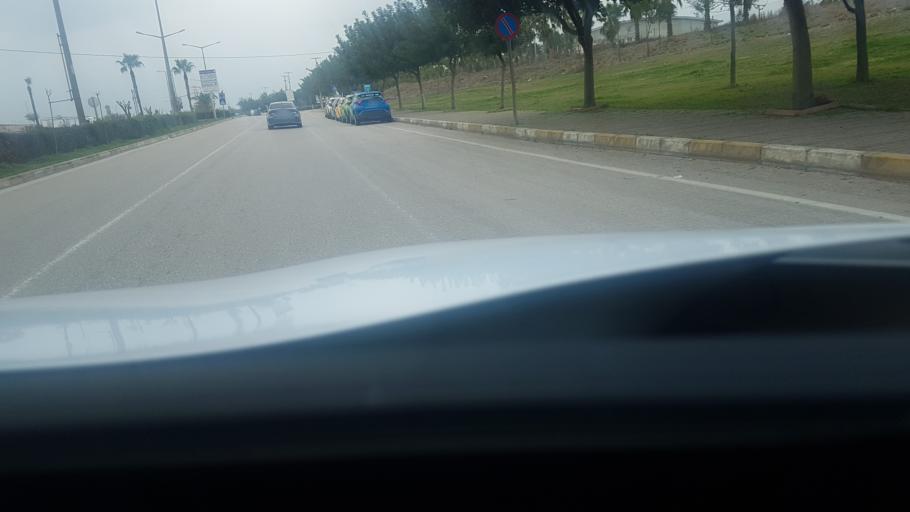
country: TR
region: Adana
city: Seyhan
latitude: 37.0550
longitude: 35.2491
